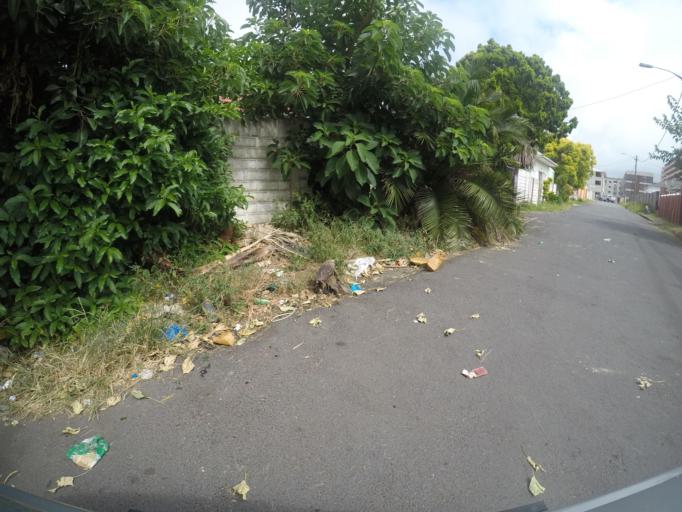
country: ZA
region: Eastern Cape
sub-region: Buffalo City Metropolitan Municipality
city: East London
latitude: -33.0005
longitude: 27.9059
